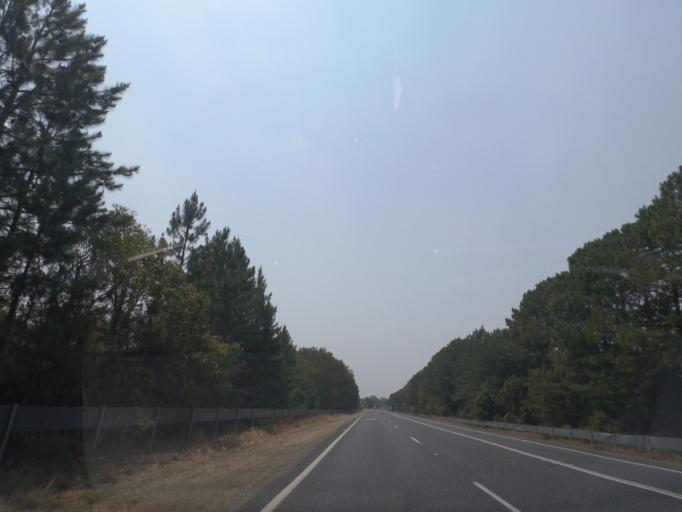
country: AU
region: New South Wales
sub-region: Ballina
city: Ballina
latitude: -28.9398
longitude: 153.4698
